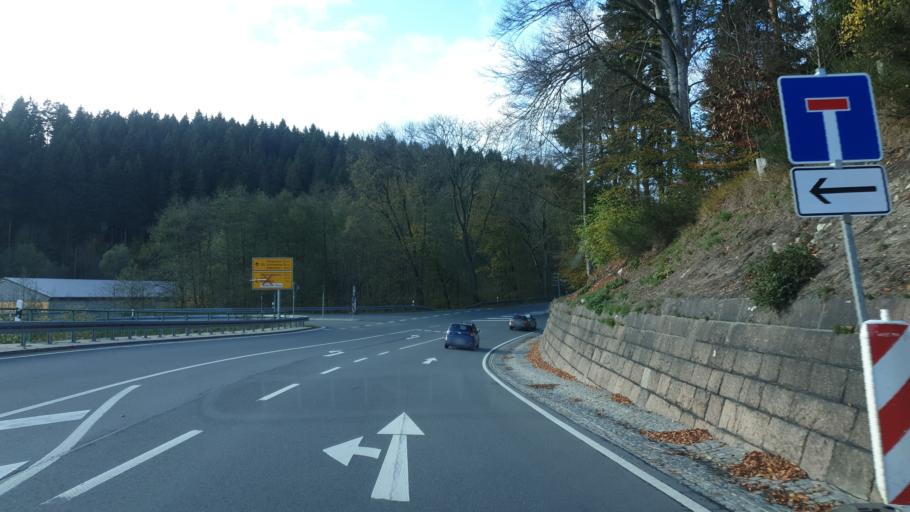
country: DE
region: Saxony
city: Sosa
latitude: 50.5163
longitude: 12.6240
